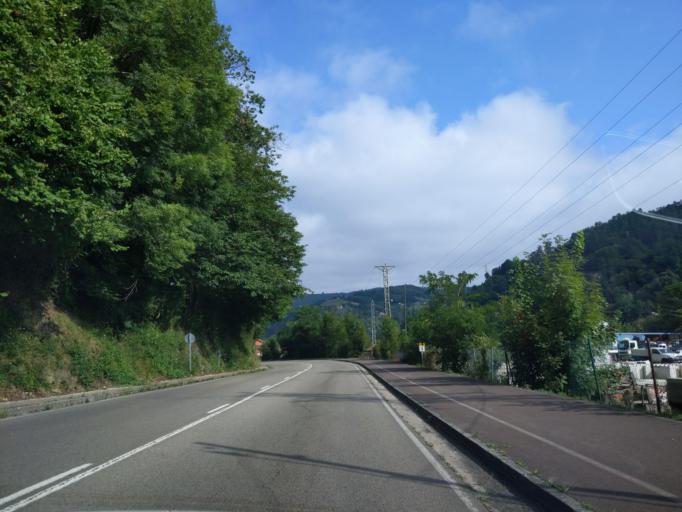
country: ES
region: Asturias
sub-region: Province of Asturias
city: El entrego
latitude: 43.2780
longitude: -5.6187
